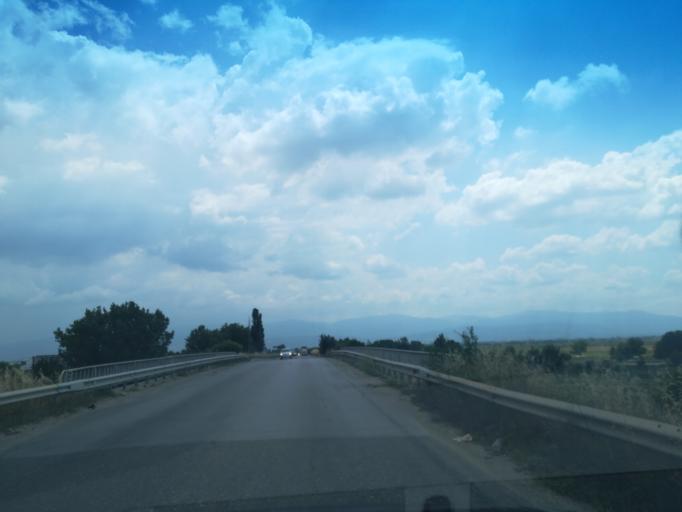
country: BG
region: Plovdiv
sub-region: Obshtina Plovdiv
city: Plovdiv
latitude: 42.1911
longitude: 24.6765
